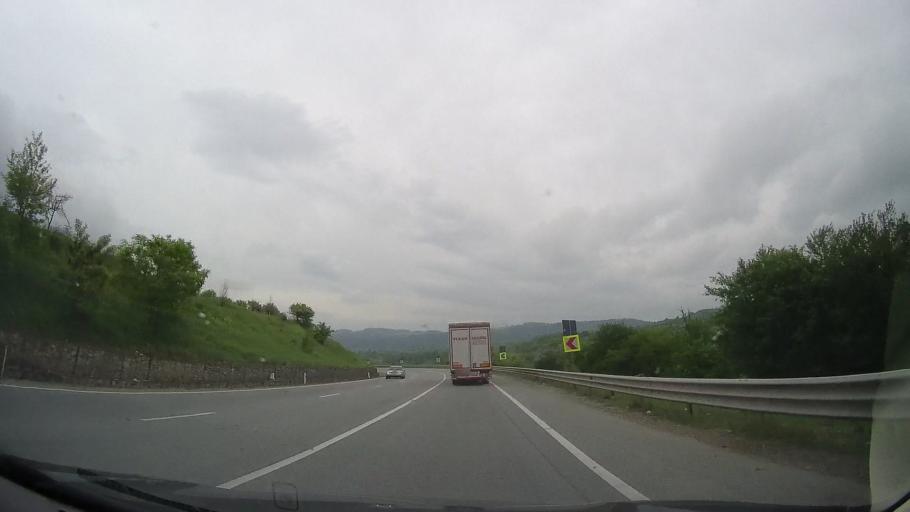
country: RO
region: Caras-Severin
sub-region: Comuna Domasnea
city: Domasnea
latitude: 45.0882
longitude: 22.3111
